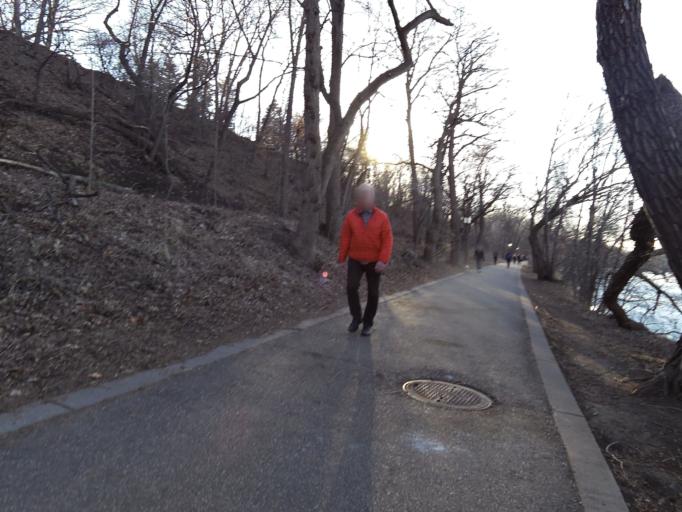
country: US
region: Minnesota
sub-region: Hennepin County
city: Richfield
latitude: 44.9156
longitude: -93.3074
